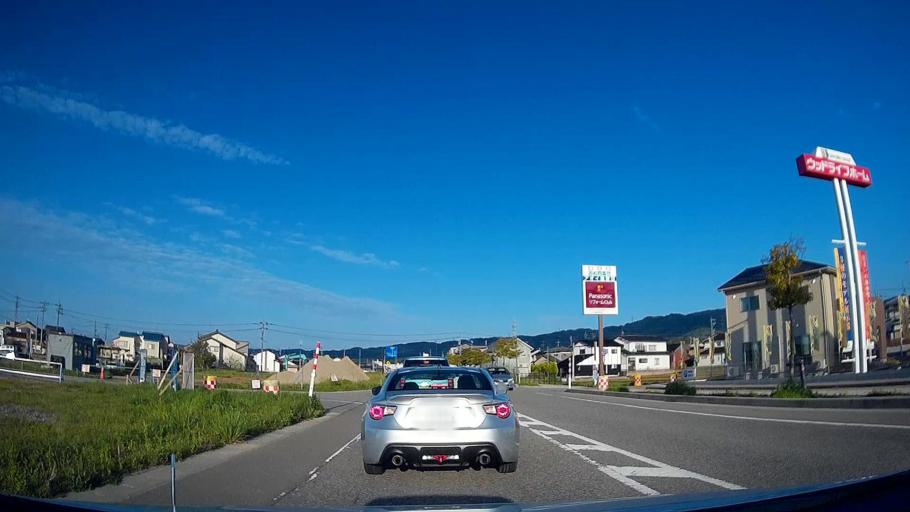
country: JP
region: Ishikawa
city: Nanao
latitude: 37.0321
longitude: 136.9642
